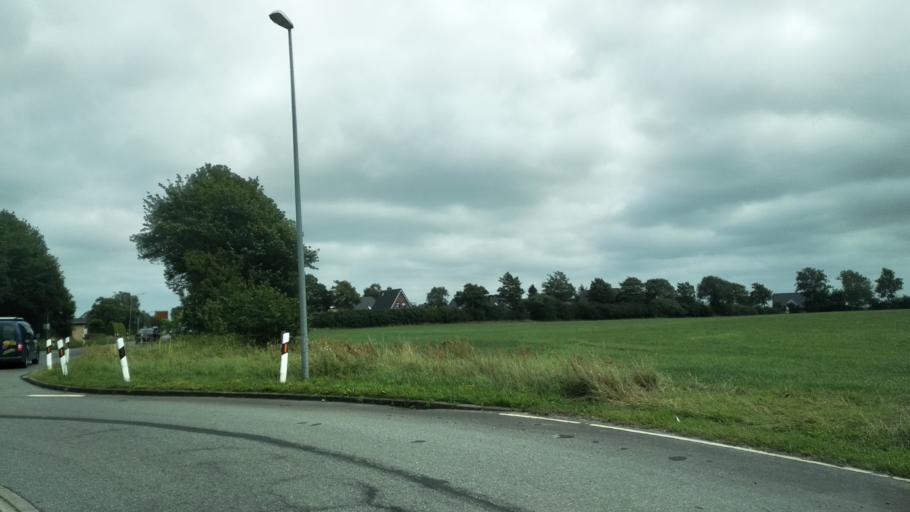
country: DE
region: Schleswig-Holstein
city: Jarplund-Weding
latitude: 54.7401
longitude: 9.4286
